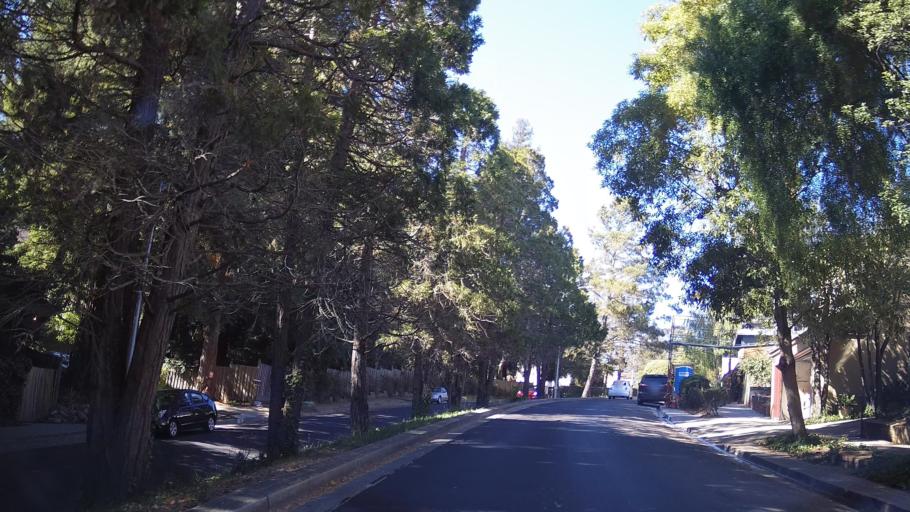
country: US
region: California
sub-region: Contra Costa County
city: Kensington
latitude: 37.9088
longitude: -122.2806
